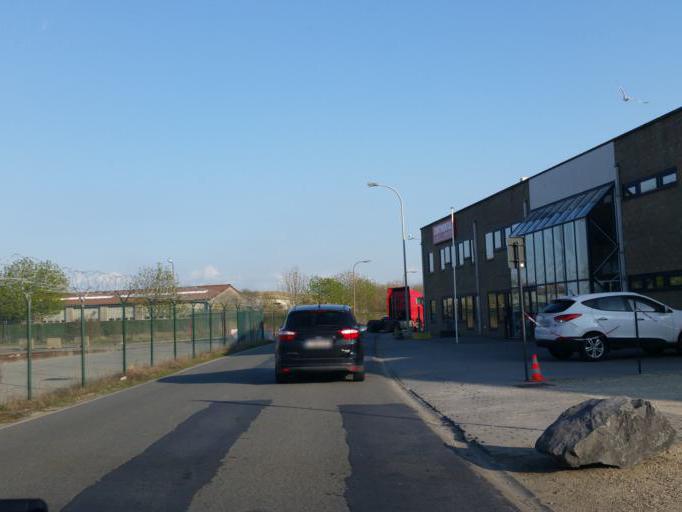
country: BE
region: Flanders
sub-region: Provincie West-Vlaanderen
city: Ostend
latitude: 51.2210
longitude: 2.9447
